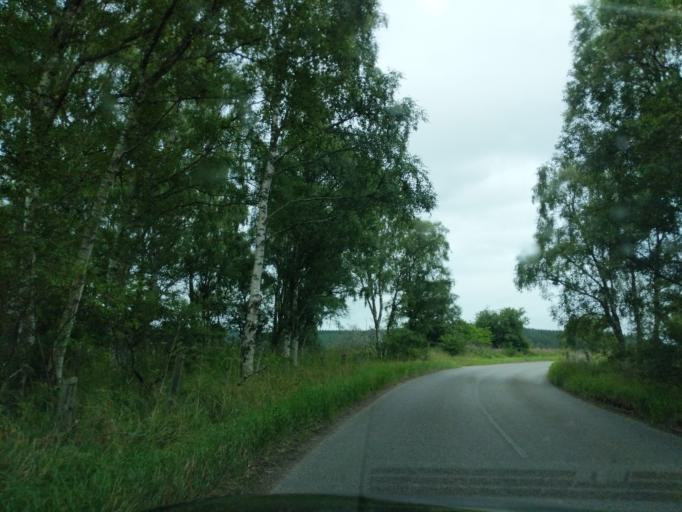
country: GB
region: Scotland
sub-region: Aberdeenshire
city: Aboyne
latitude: 57.1090
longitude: -2.8130
